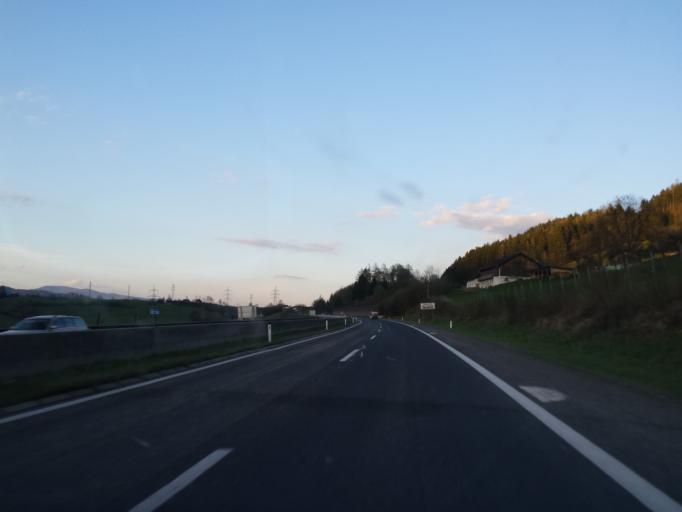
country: AT
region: Styria
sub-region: Politischer Bezirk Bruck-Muerzzuschlag
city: Kindberg
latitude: 47.5118
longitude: 15.4704
